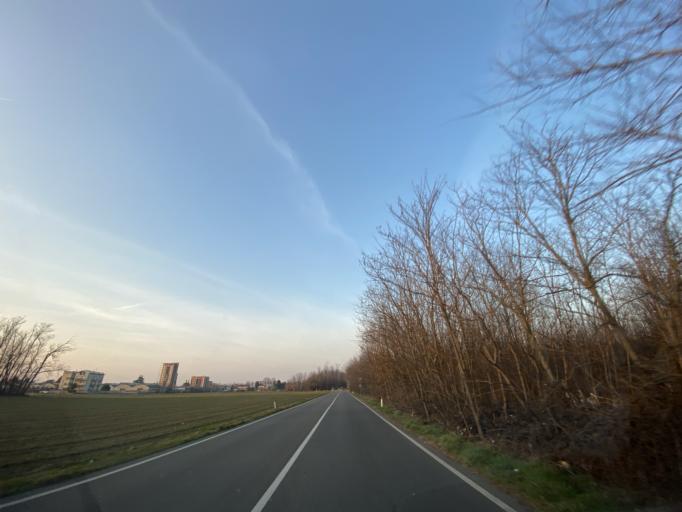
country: IT
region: Lombardy
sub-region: Citta metropolitana di Milano
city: Garbagnate Milanese
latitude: 45.5838
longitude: 9.0633
